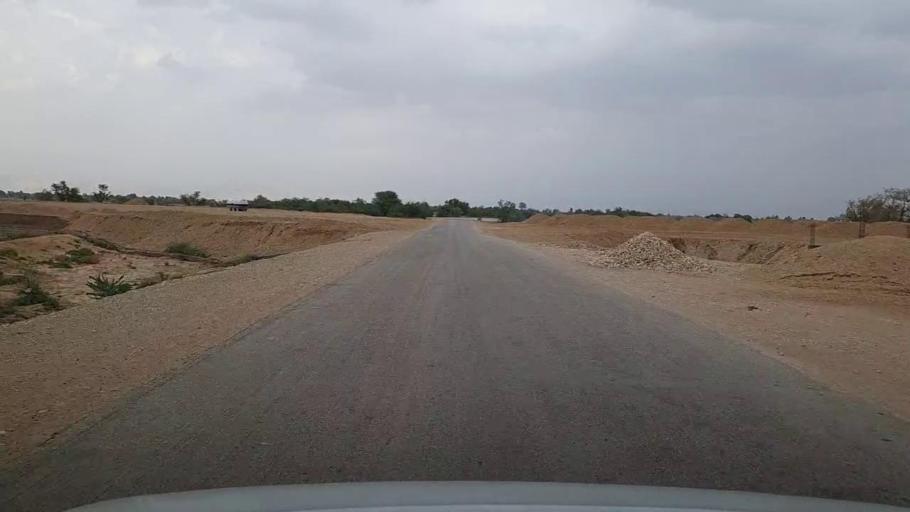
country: PK
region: Sindh
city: Sehwan
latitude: 26.3394
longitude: 67.7267
